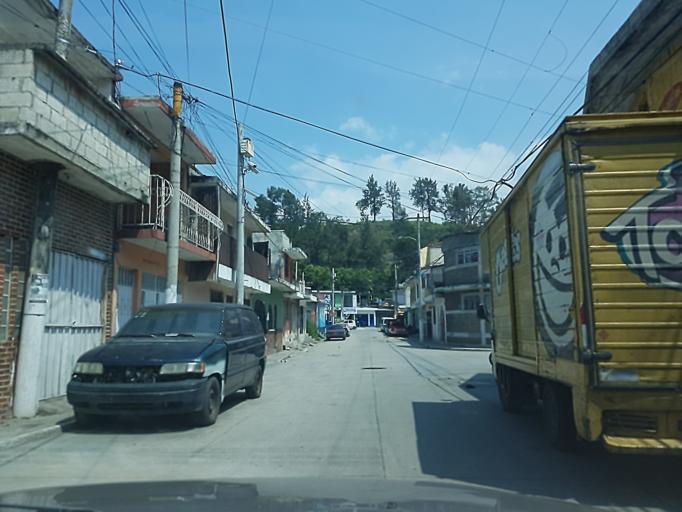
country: GT
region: Guatemala
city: Petapa
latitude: 14.5235
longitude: -90.5487
